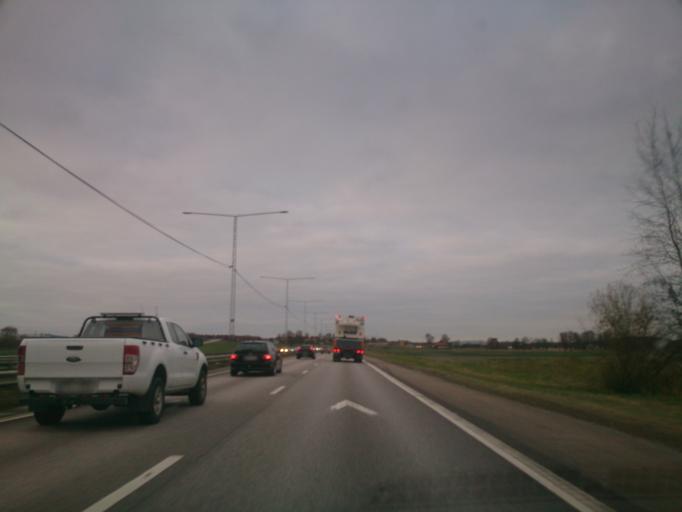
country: SE
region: Stockholm
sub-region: Sigtuna Kommun
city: Rosersberg
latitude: 59.5605
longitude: 17.8980
